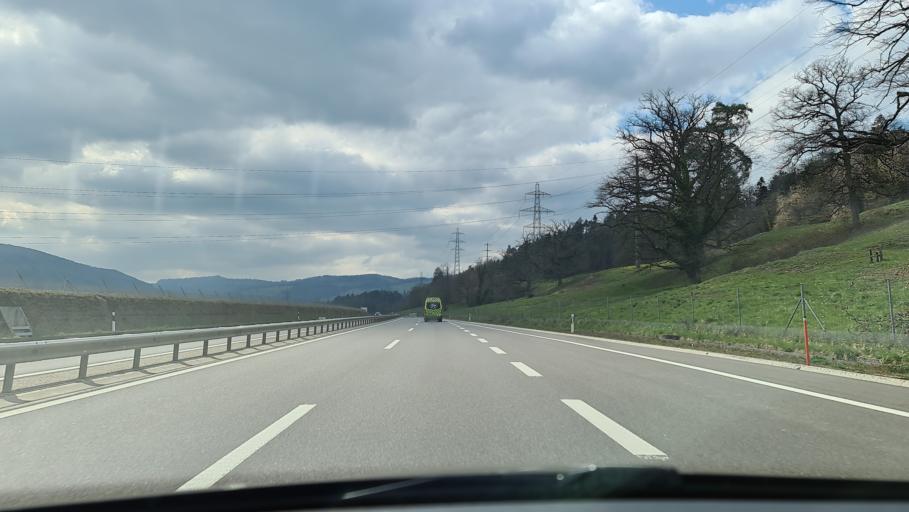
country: CH
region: Jura
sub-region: Delemont District
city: Bassecourt
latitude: 47.3458
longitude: 7.2541
